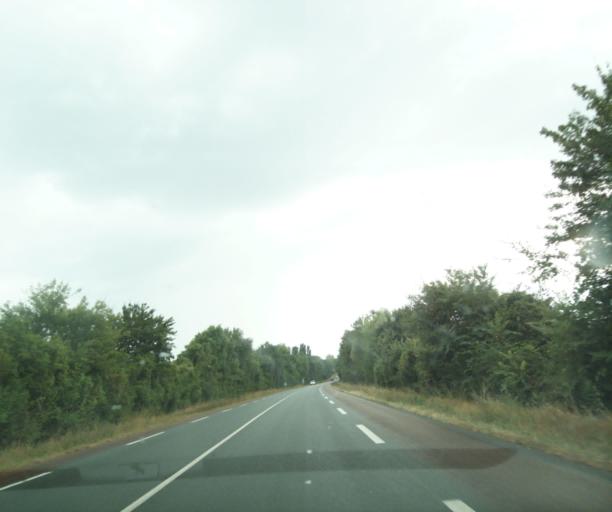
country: FR
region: Poitou-Charentes
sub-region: Departement de la Charente-Maritime
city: Cabariot
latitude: 45.9440
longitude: -0.8647
